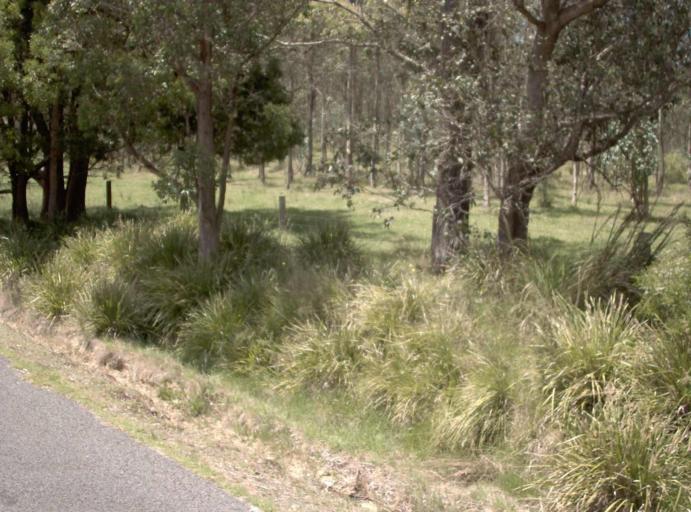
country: AU
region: New South Wales
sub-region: Bombala
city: Bombala
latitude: -37.4066
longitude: 149.0107
